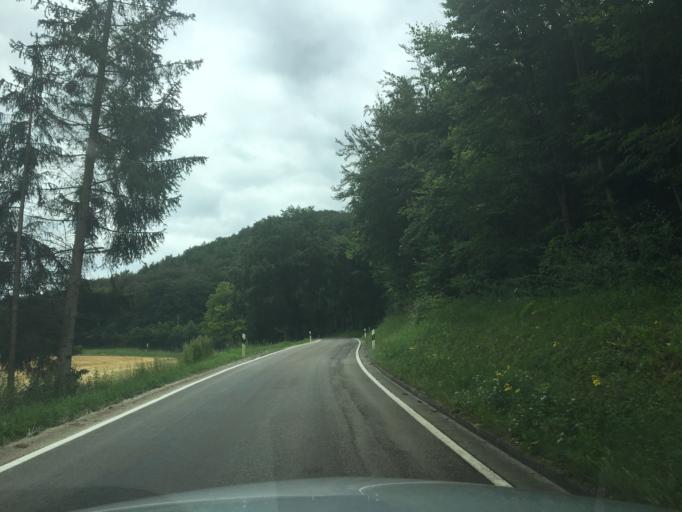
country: DE
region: Bavaria
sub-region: Regierungsbezirk Mittelfranken
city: Greding
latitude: 49.0140
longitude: 11.3664
